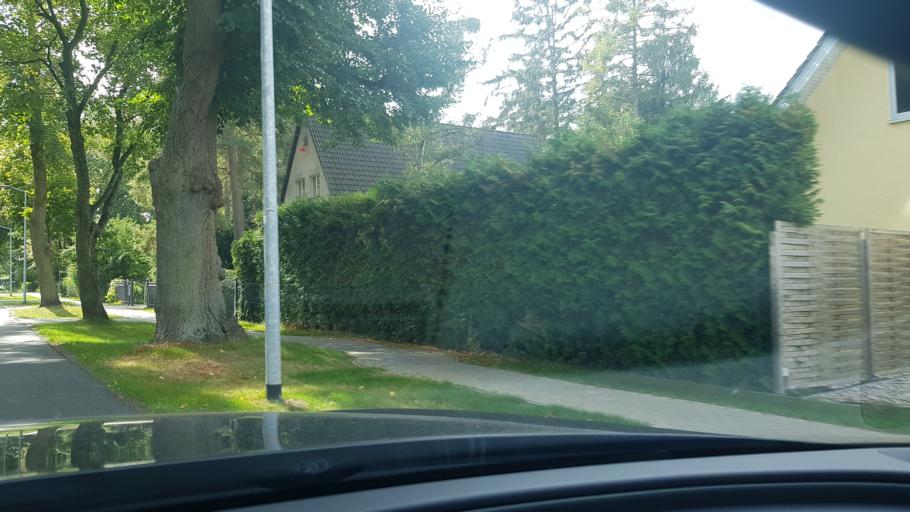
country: DE
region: Brandenburg
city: Brieselang
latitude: 52.5942
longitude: 12.9949
